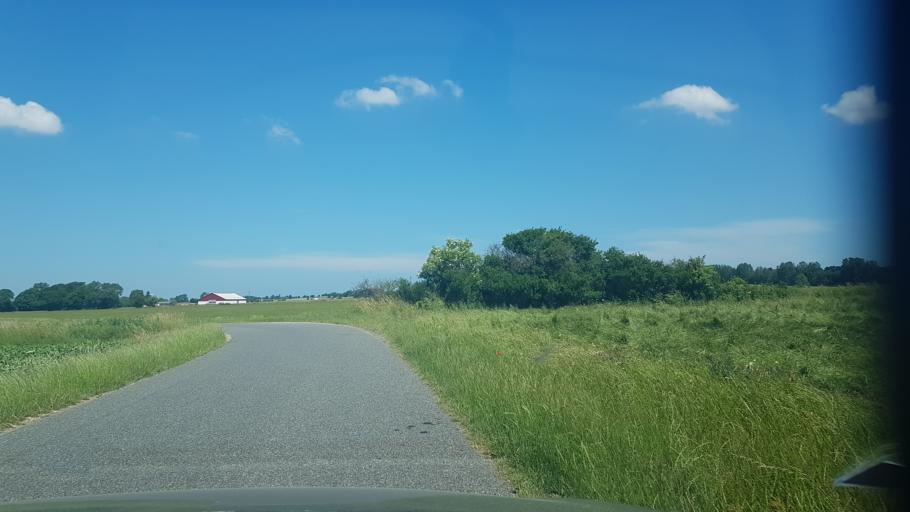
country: DK
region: Zealand
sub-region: Kalundborg Kommune
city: Svebolle
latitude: 55.6945
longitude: 11.2992
